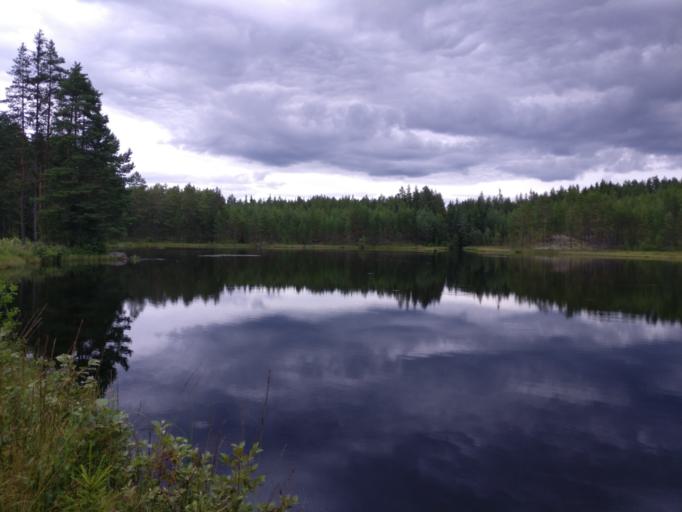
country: SE
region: Vaermland
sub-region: Hagfors Kommun
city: Ekshaerad
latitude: 60.2919
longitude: 13.4691
